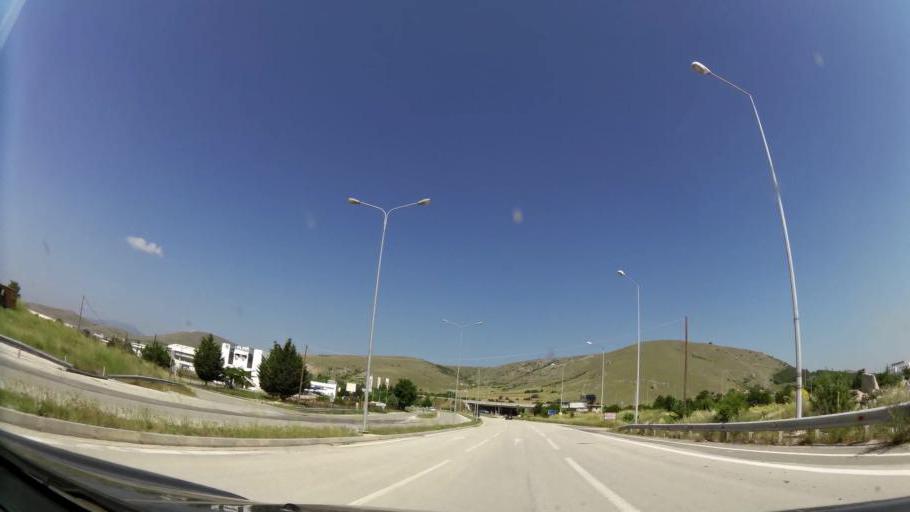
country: GR
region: West Macedonia
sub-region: Nomos Kozanis
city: Koila
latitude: 40.3449
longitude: 21.8019
